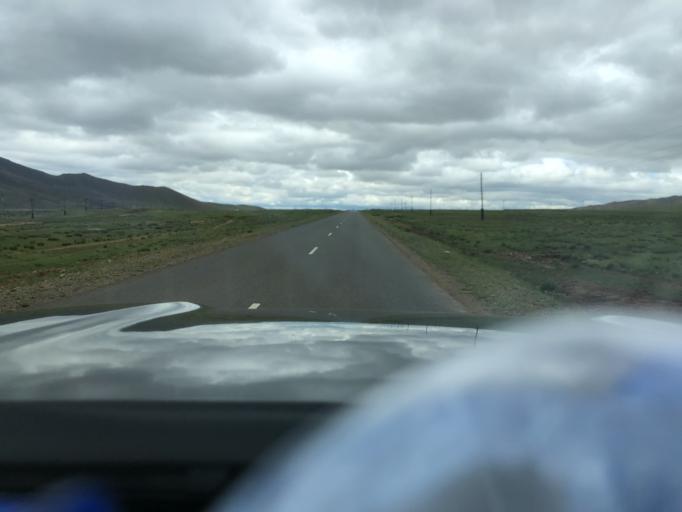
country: MN
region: Central Aimak
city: Ihsueuej
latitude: 48.0797
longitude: 106.5840
